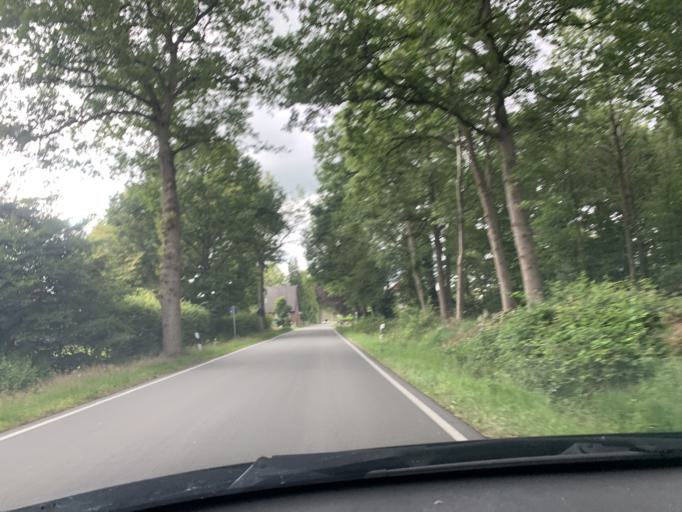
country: DE
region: Lower Saxony
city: Westerstede
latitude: 53.2207
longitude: 7.9085
